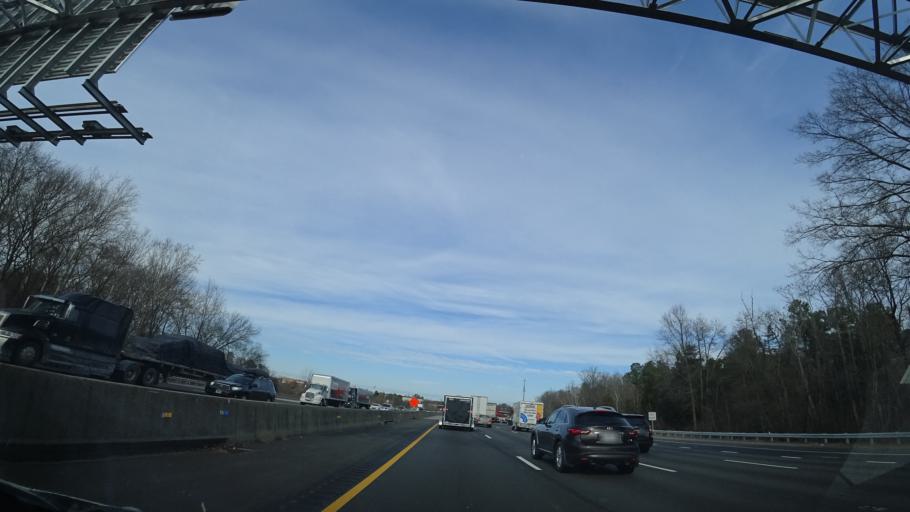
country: US
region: Virginia
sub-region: Henrico County
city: Chamberlayne
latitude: 37.6794
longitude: -77.4505
